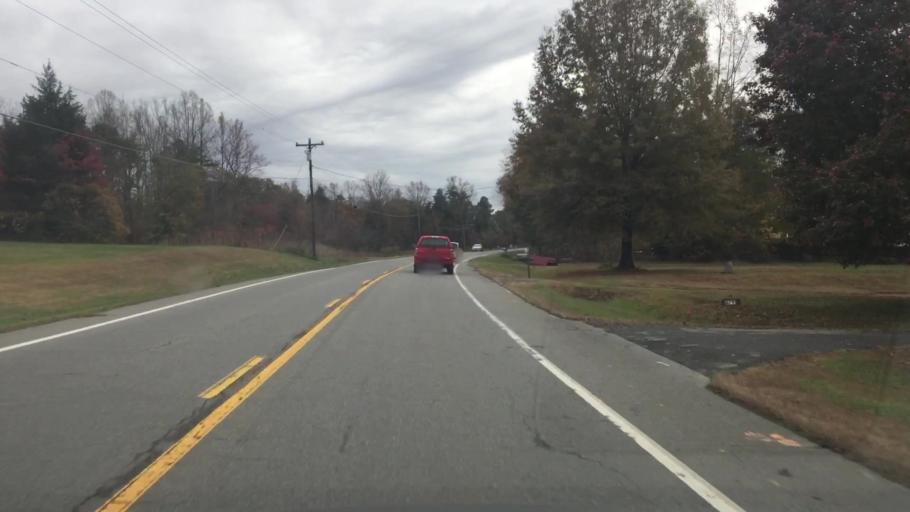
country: US
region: North Carolina
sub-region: Rockingham County
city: Reidsville
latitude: 36.3013
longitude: -79.7233
